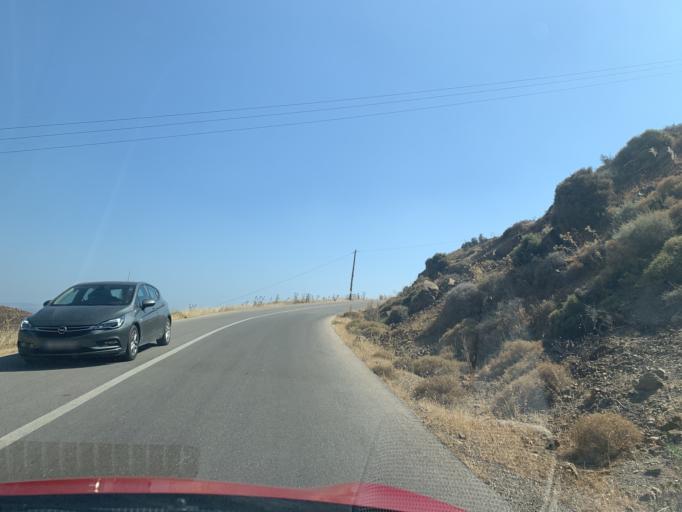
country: GR
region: North Aegean
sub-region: Chios
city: Vrontados
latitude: 38.4807
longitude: 25.8941
